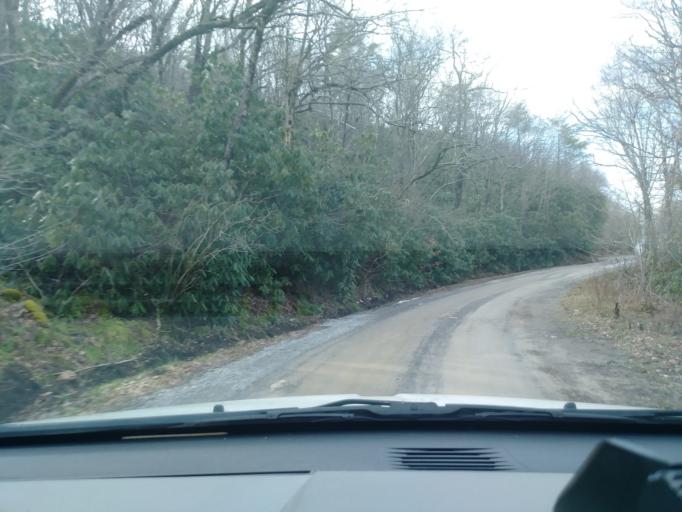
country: US
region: Tennessee
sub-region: Greene County
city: Tusculum
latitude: 36.0299
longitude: -82.7114
